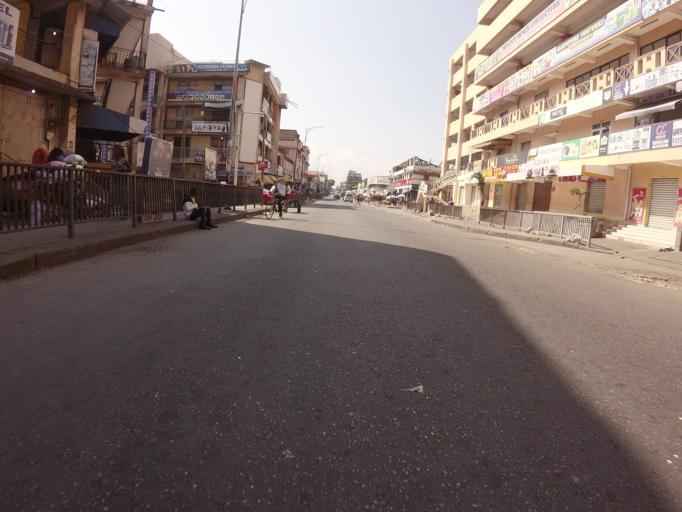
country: GH
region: Greater Accra
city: Accra
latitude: 5.5469
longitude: -0.2069
